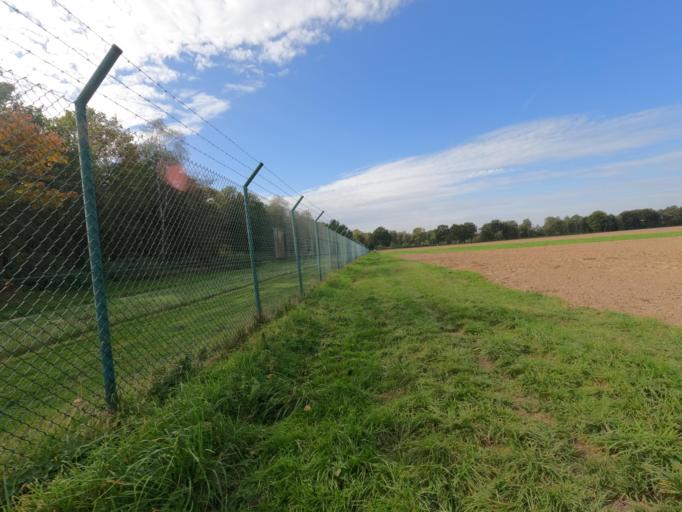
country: DE
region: North Rhine-Westphalia
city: Geilenkirchen
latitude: 50.9652
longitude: 6.0605
